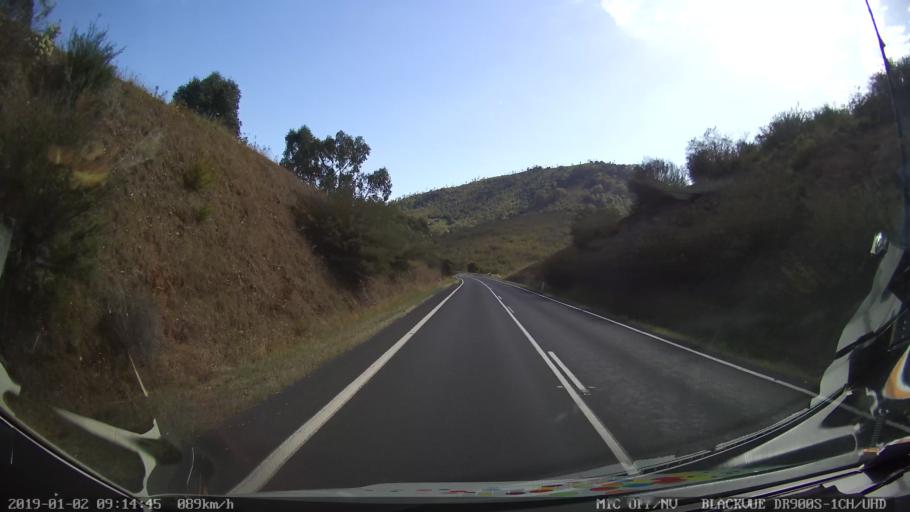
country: AU
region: New South Wales
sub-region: Tumut Shire
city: Tumut
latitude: -35.4734
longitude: 148.2770
